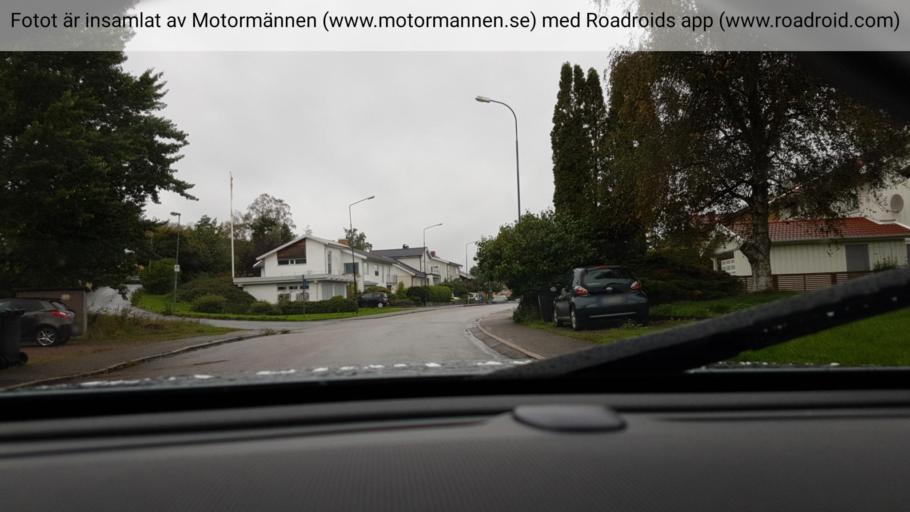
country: SE
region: Vaestra Goetaland
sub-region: Molndal
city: Moelndal
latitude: 57.6719
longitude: 11.9971
